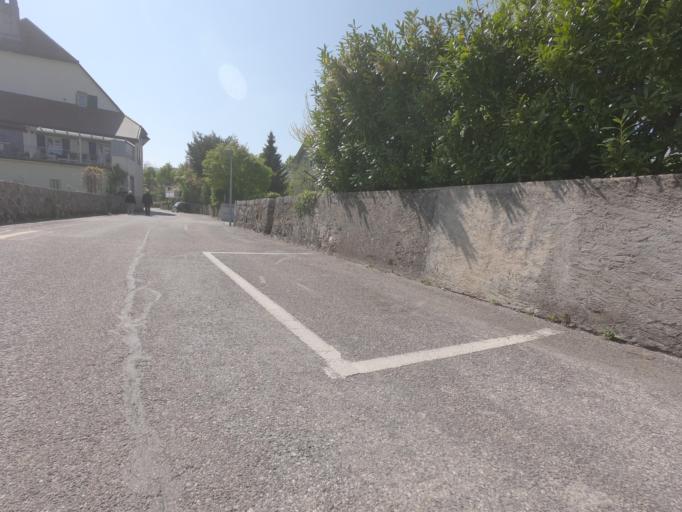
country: CH
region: Neuchatel
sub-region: Neuchatel District
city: Le Landeron
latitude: 47.0575
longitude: 7.0735
